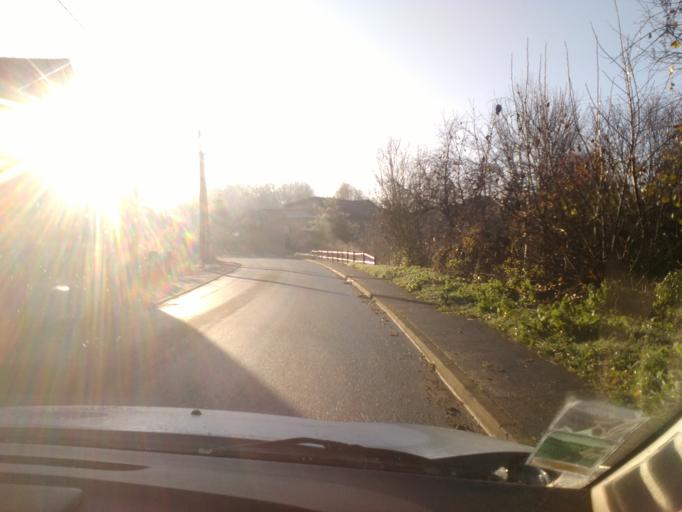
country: FR
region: Lorraine
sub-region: Departement des Vosges
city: Darnieulles
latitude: 48.1595
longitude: 6.2294
